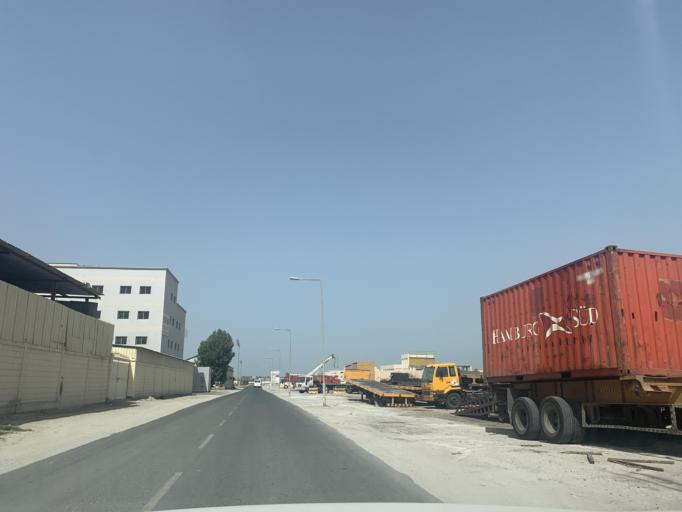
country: BH
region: Northern
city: Sitrah
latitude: 26.1540
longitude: 50.6228
